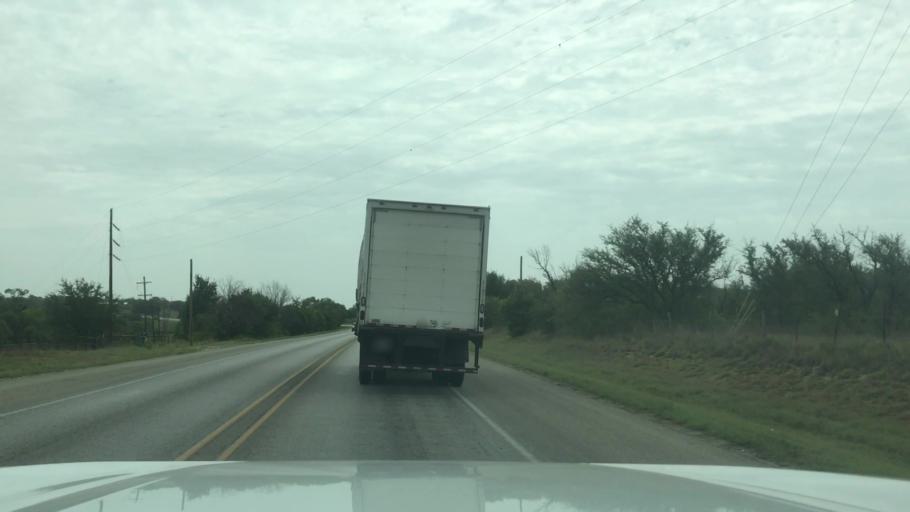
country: US
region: Texas
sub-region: Erath County
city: Dublin
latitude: 32.0895
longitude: -98.4374
